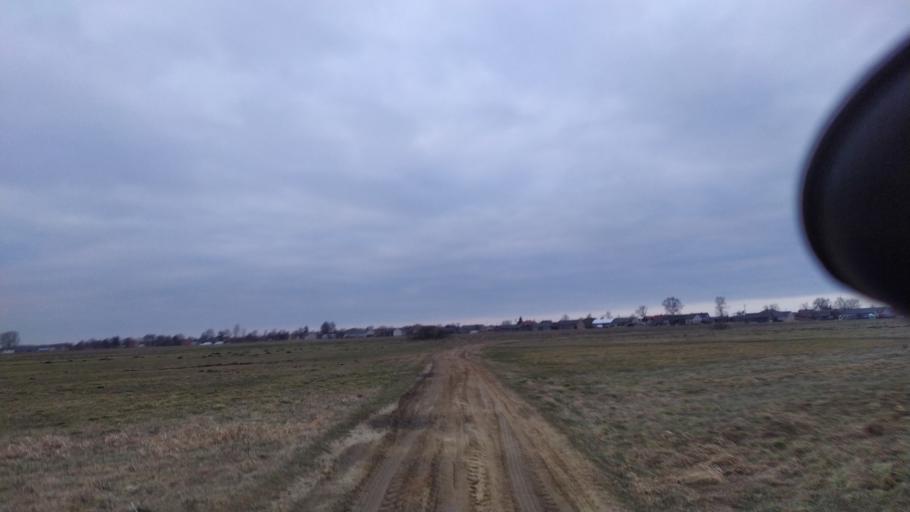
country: PL
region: Lublin Voivodeship
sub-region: Powiat lubartowski
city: Abramow
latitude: 51.4358
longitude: 22.2937
